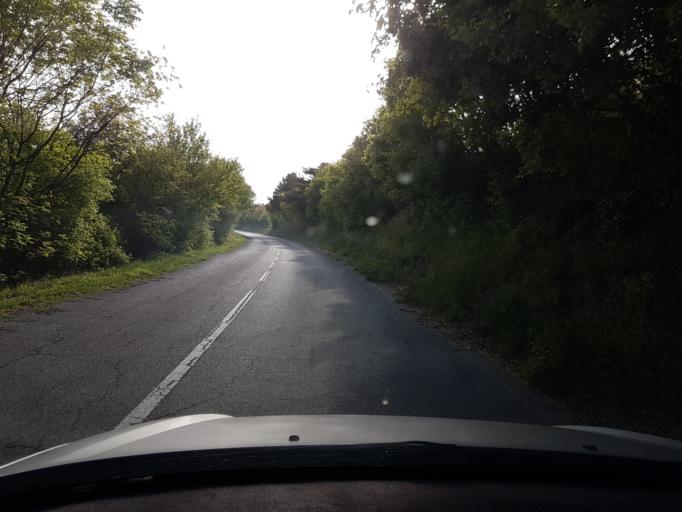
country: IT
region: Friuli Venezia Giulia
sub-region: Provincia di Trieste
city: Dolina
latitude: 45.5886
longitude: 13.8573
